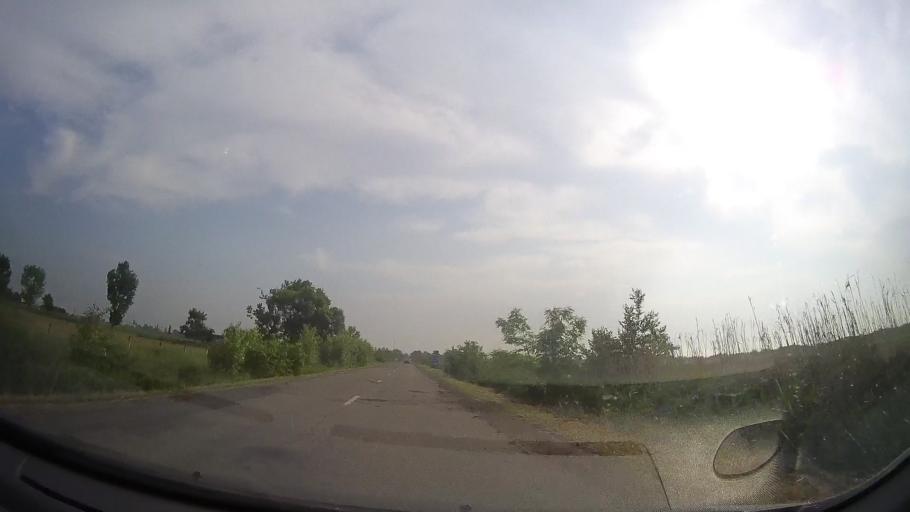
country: RO
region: Timis
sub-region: Comuna Peciu Nou
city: Peciu Nou
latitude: 45.5941
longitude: 21.0431
